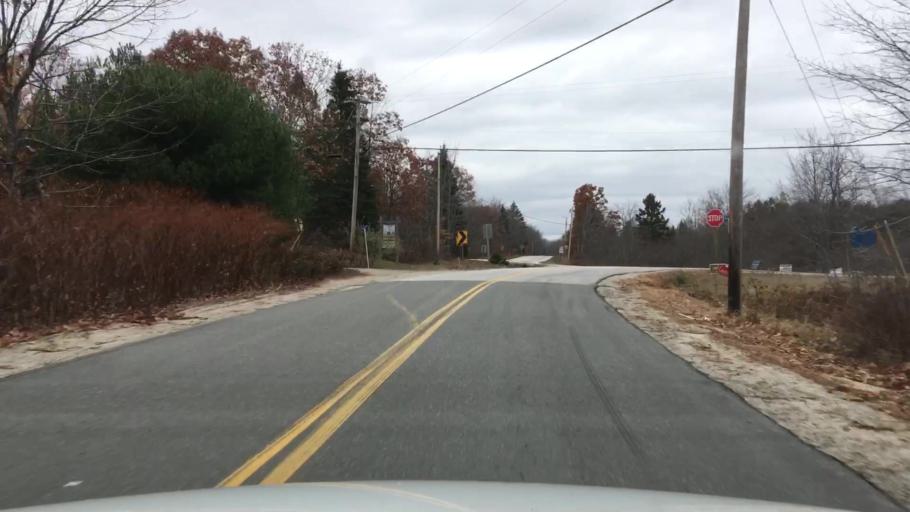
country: US
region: Maine
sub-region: Hancock County
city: Penobscot
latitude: 44.4626
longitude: -68.6372
